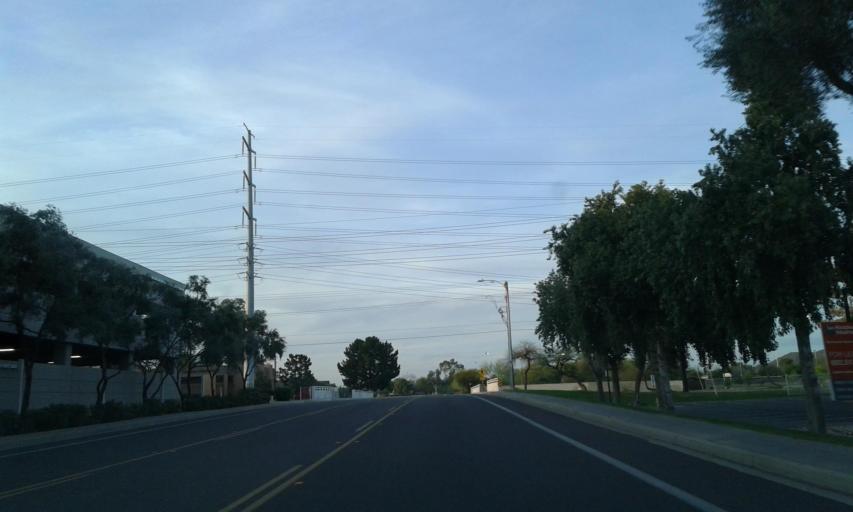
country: US
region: Arizona
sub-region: Maricopa County
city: Glendale
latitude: 33.5704
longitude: -112.1122
